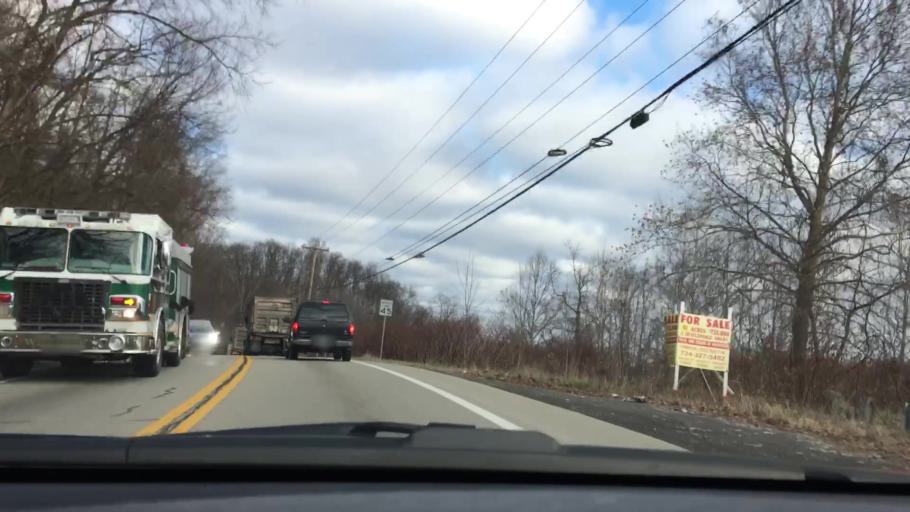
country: US
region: Pennsylvania
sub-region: Westmoreland County
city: Trafford
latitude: 40.3815
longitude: -79.7762
